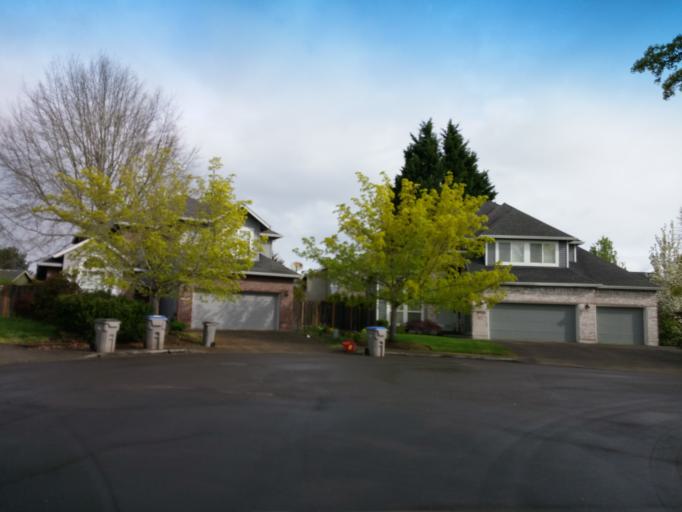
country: US
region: Oregon
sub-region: Washington County
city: Oak Hills
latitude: 45.5373
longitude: -122.8426
